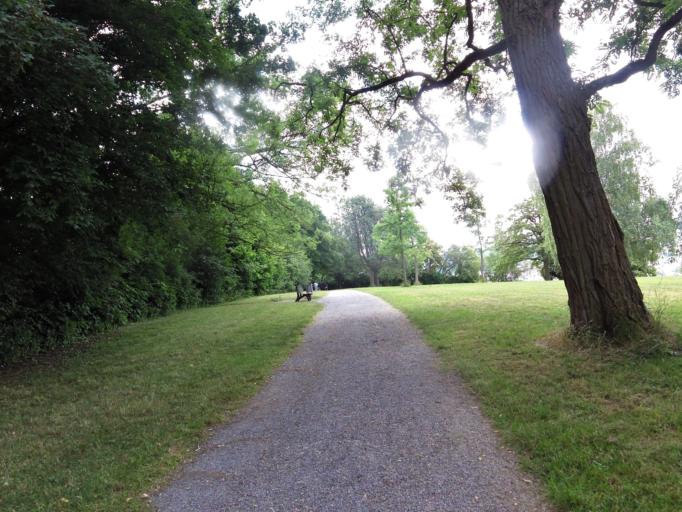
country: DE
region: Bavaria
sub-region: Regierungsbezirk Unterfranken
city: Wuerzburg
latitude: 49.7719
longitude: 9.9539
